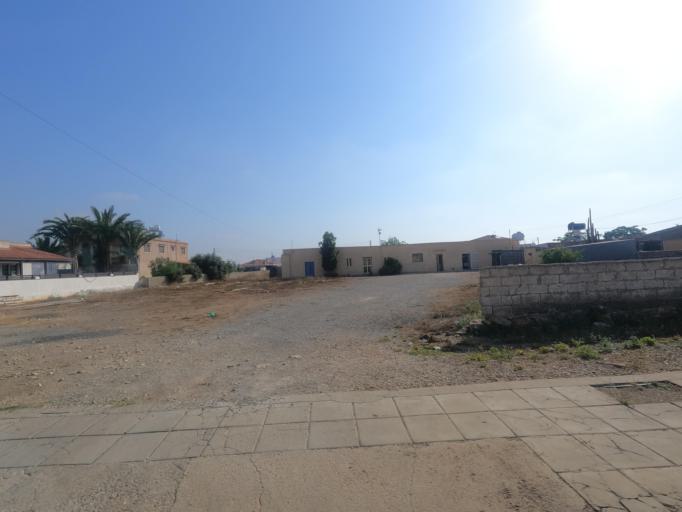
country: CY
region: Ammochostos
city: Avgorou
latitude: 35.0409
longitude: 33.8354
